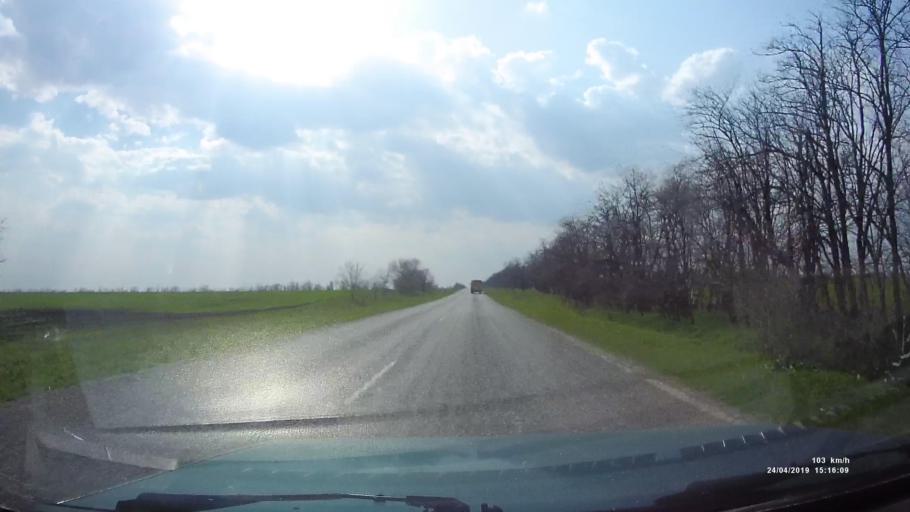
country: RU
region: Rostov
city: Remontnoye
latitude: 46.5462
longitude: 43.2199
